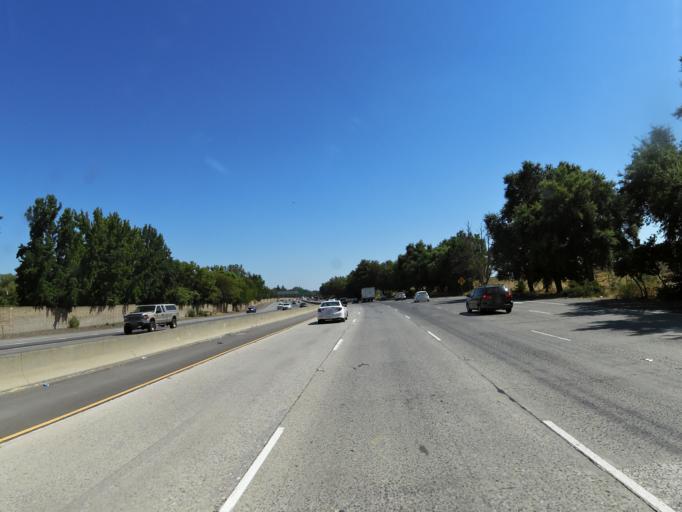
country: US
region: California
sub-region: Yolo County
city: West Sacramento
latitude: 38.5553
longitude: -121.5129
